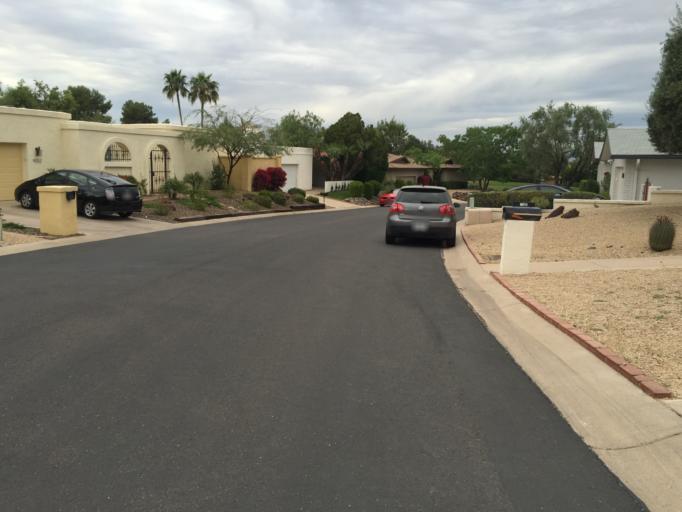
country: US
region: Arizona
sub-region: Maricopa County
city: Paradise Valley
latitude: 33.5698
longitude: -112.0151
